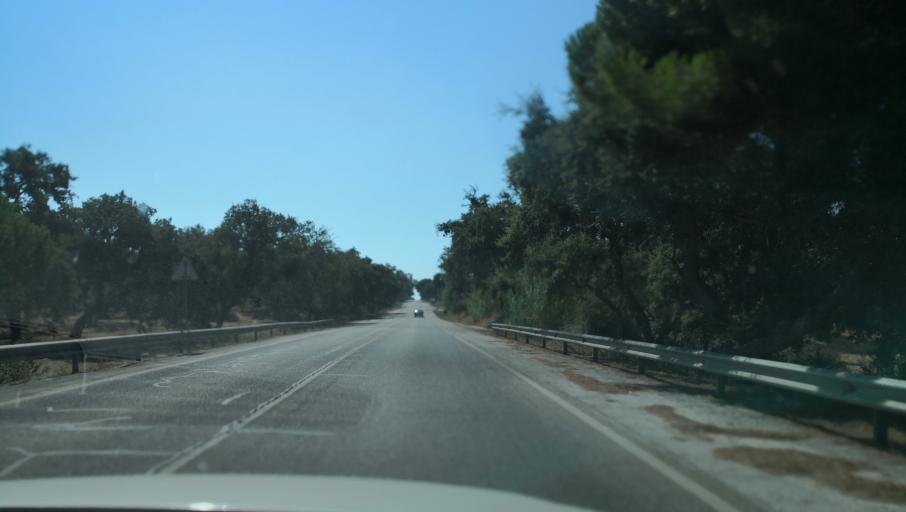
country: PT
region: Setubal
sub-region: Alcacer do Sal
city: Alcacer do Sal
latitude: 38.3624
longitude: -8.5129
